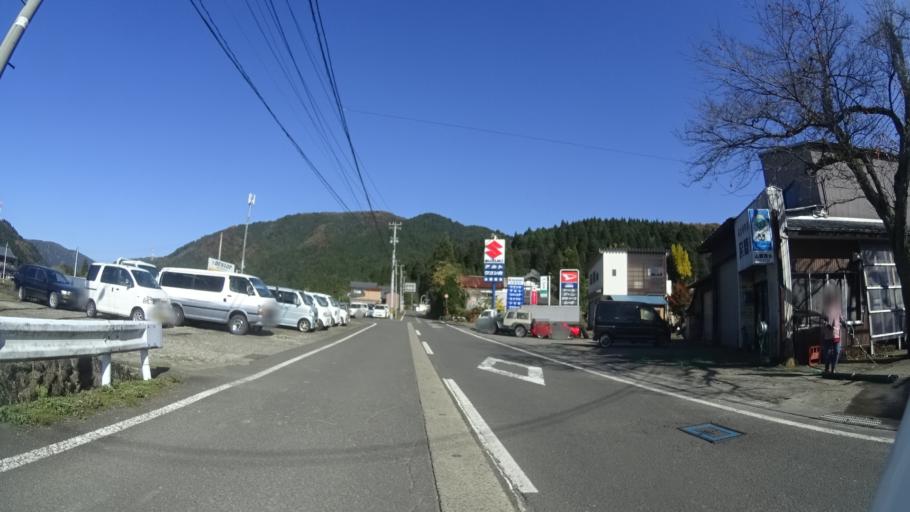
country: JP
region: Fukui
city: Ono
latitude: 35.8992
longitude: 136.3545
